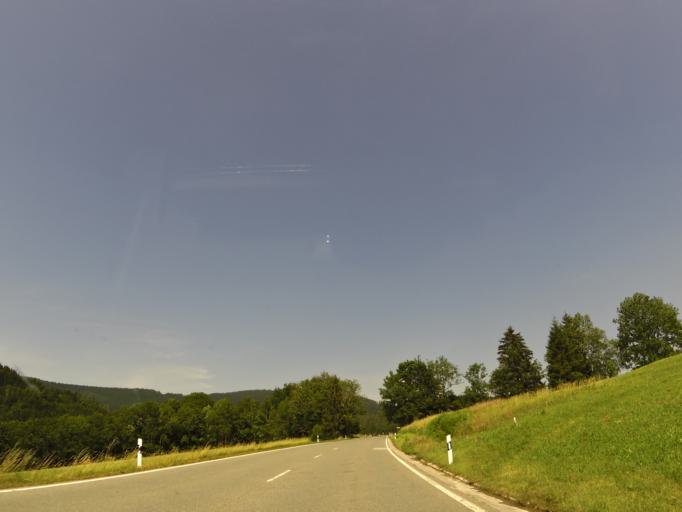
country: DE
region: Bavaria
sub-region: Upper Bavaria
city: Ruhpolding
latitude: 47.7527
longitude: 12.6786
